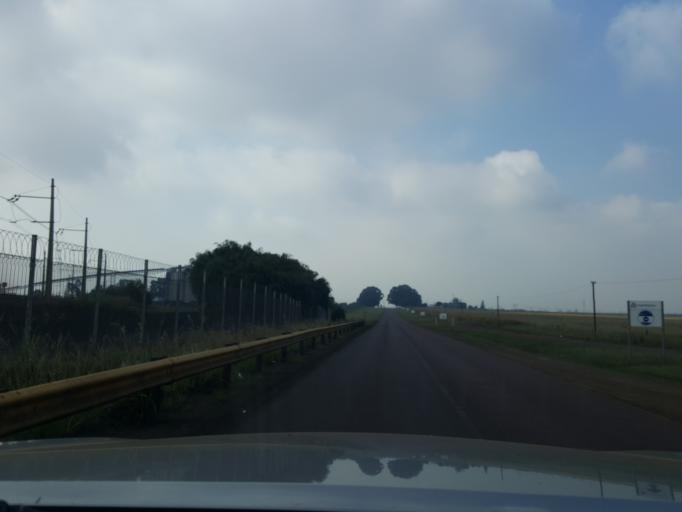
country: ZA
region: Mpumalanga
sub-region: Nkangala District Municipality
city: Middelburg
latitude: -25.9727
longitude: 29.4500
